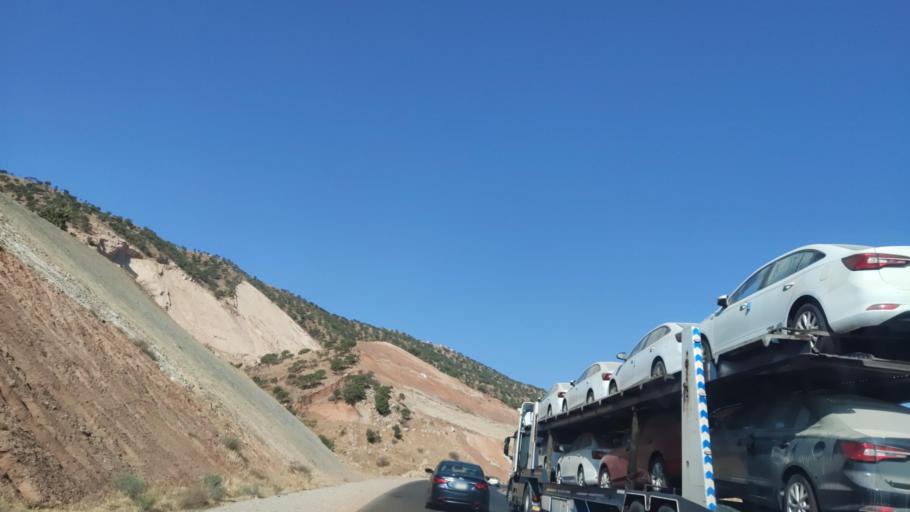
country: IQ
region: Arbil
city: Shaqlawah
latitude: 36.4351
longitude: 44.2979
